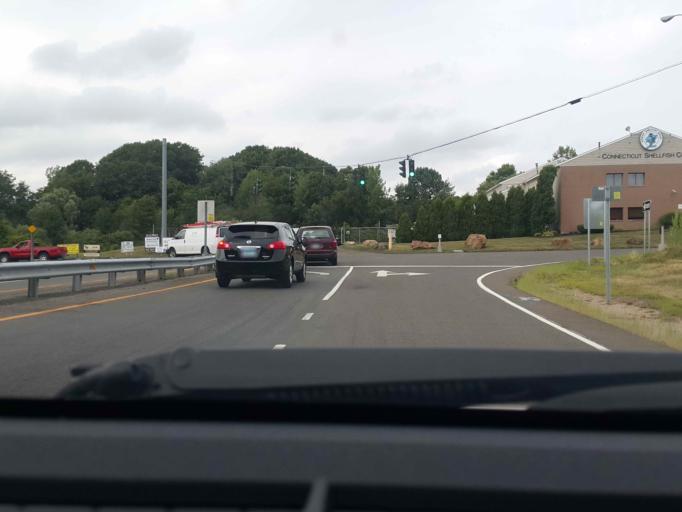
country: US
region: Connecticut
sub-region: New Haven County
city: North Branford
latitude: 41.2973
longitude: -72.7580
